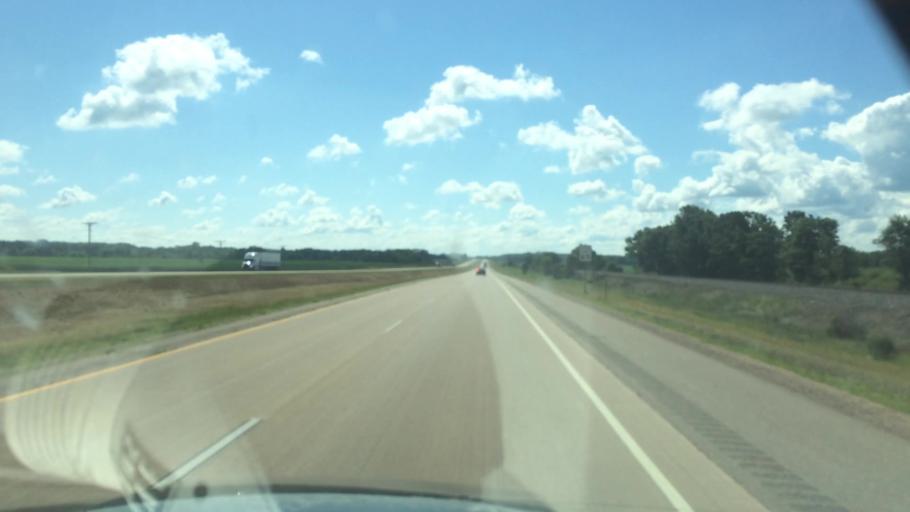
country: US
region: Wisconsin
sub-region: Portage County
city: Amherst
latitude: 44.4933
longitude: -89.3647
